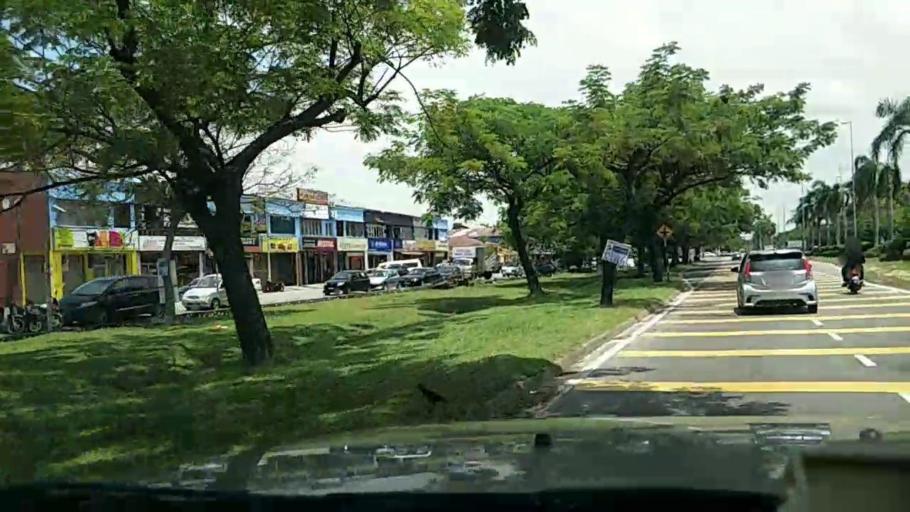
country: MY
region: Putrajaya
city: Putrajaya
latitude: 2.9500
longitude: 101.6170
